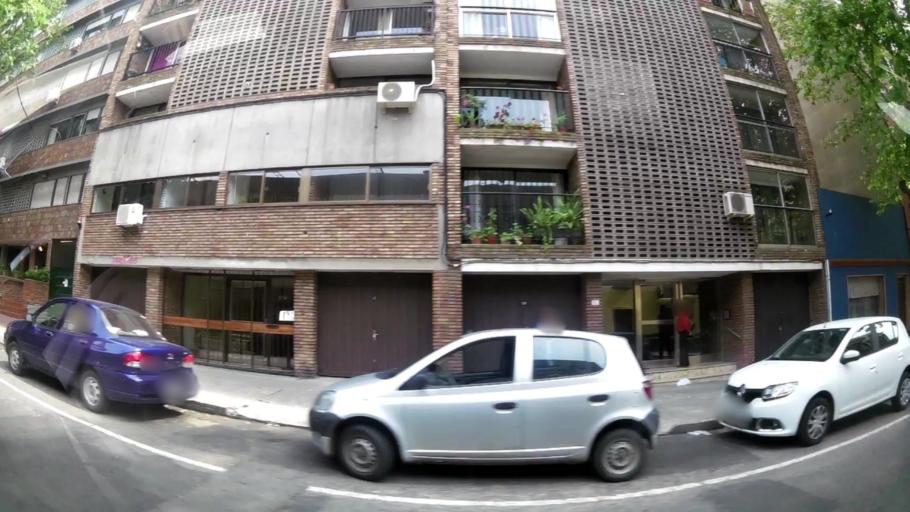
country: UY
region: Montevideo
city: Montevideo
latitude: -34.9080
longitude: -56.1854
